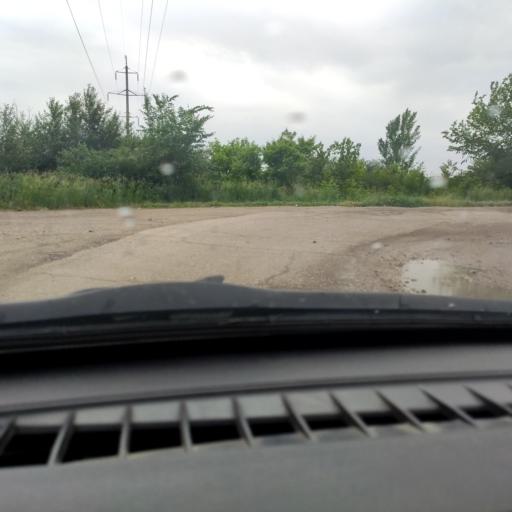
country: RU
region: Samara
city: Tol'yatti
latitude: 53.5870
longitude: 49.4351
